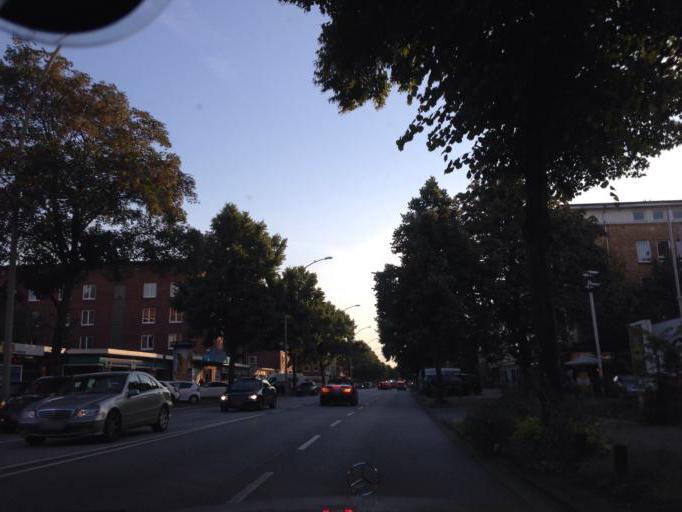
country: DE
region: Hamburg
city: Hamburg
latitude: 53.5687
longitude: 10.0245
